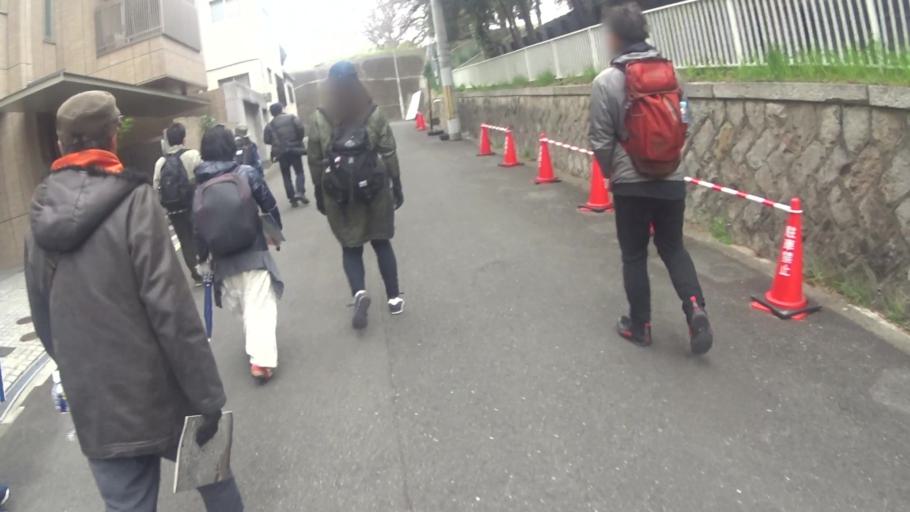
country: JP
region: Osaka
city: Osaka-shi
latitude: 34.6734
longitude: 135.5286
